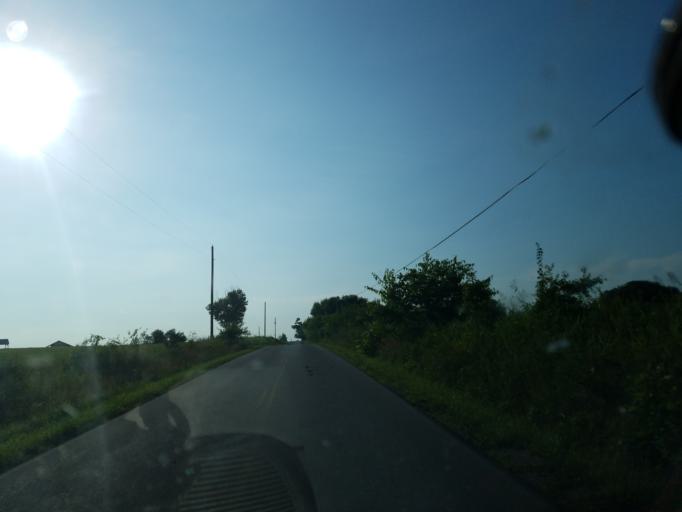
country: US
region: Ohio
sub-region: Adams County
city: West Union
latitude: 38.8803
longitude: -83.4921
